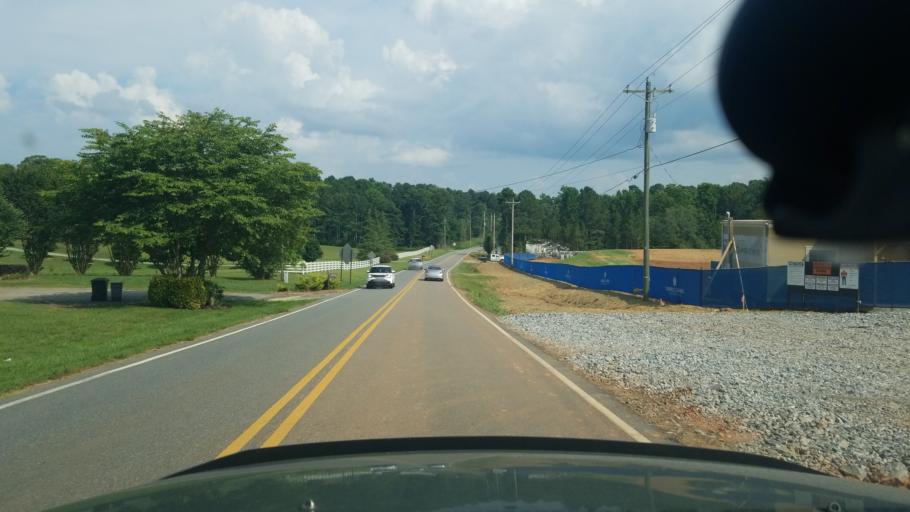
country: US
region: Georgia
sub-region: Hall County
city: Flowery Branch
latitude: 34.2644
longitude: -83.9987
